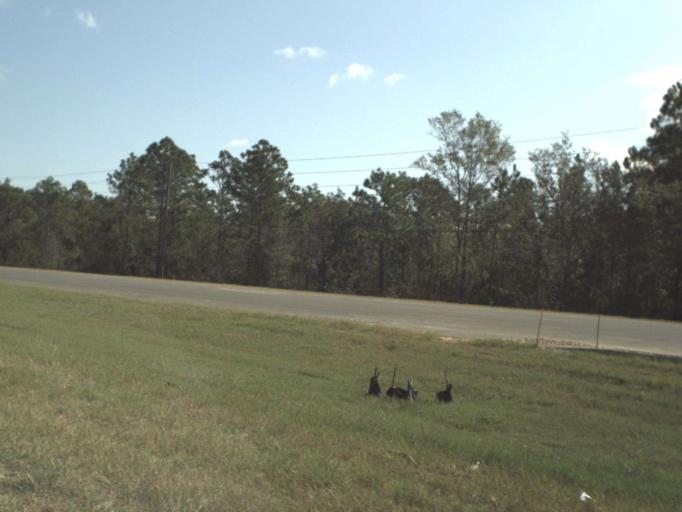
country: US
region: Florida
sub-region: Walton County
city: Freeport
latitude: 30.4471
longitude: -86.1339
